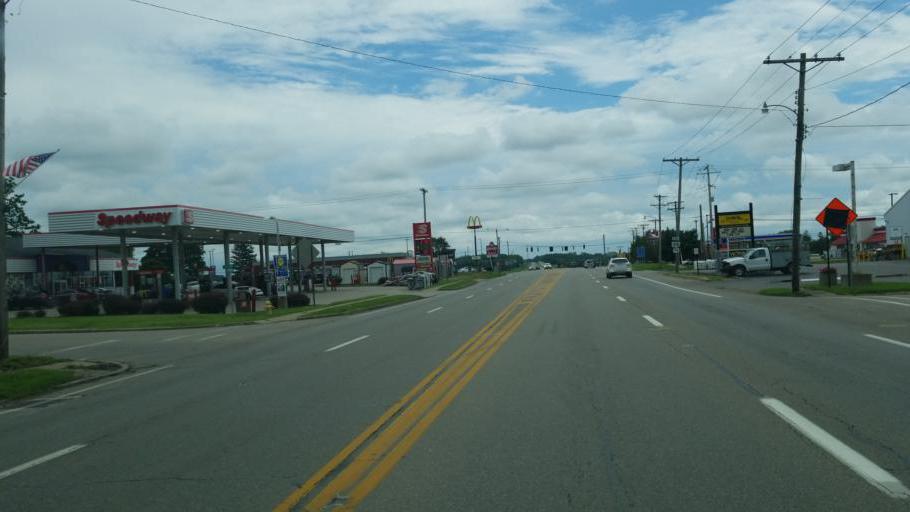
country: US
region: Ohio
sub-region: Pickaway County
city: South Bloomfield
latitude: 39.7165
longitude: -82.9869
